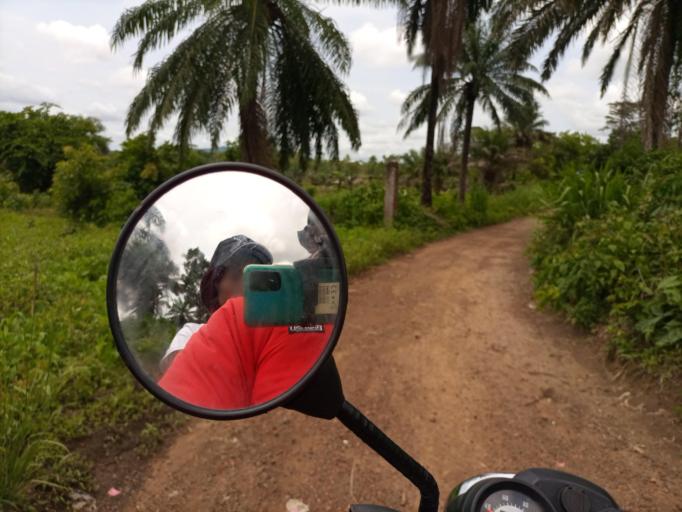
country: SL
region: Southern Province
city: Baoma
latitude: 7.9797
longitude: -11.7129
